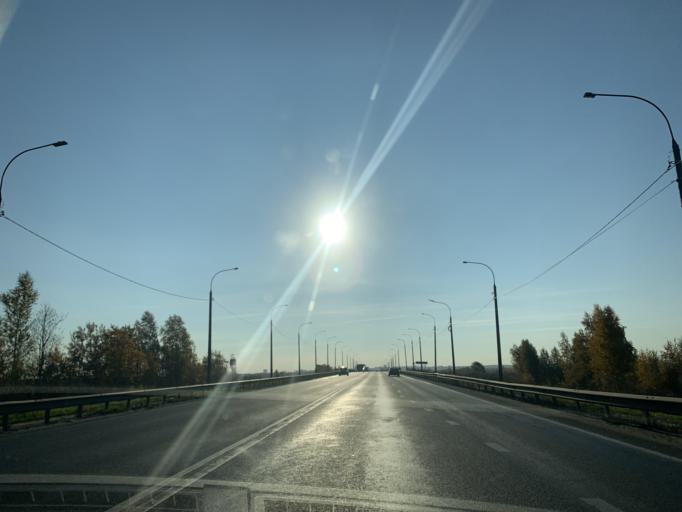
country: RU
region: Jaroslavl
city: Yaroslavl
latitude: 57.6306
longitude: 39.7538
